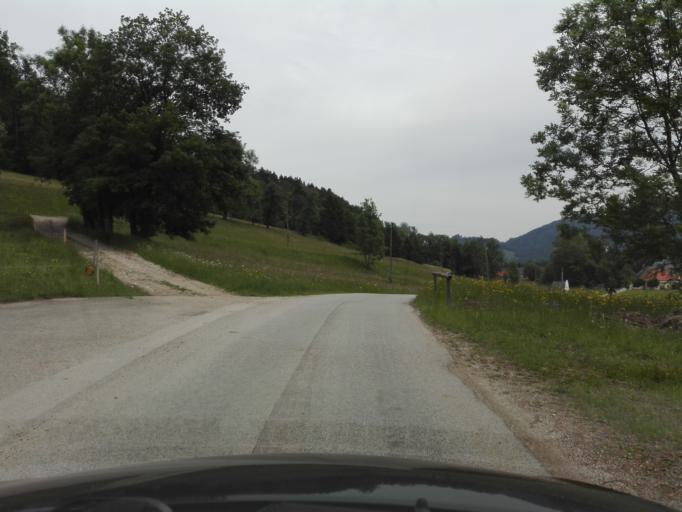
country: AT
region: Upper Austria
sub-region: Politischer Bezirk Gmunden
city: Scharnstein
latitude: 47.9148
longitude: 13.9571
